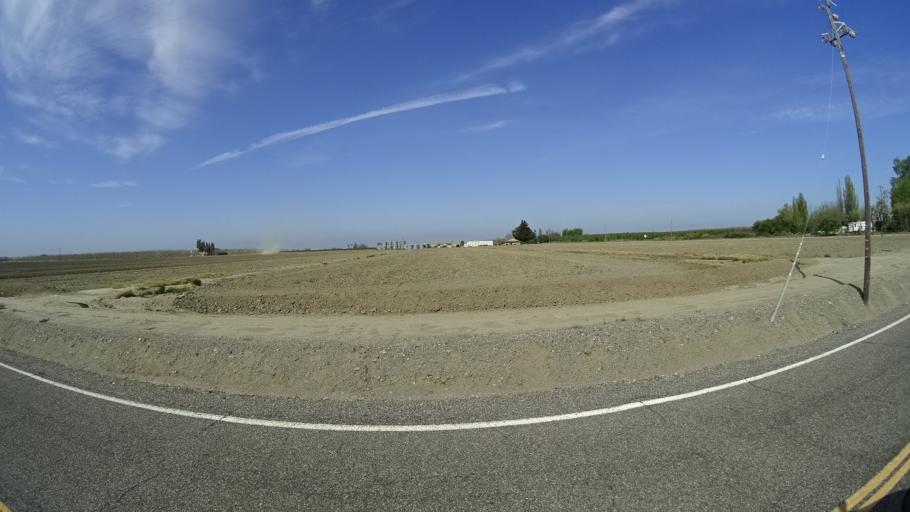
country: US
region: California
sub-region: Glenn County
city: Hamilton City
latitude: 39.6263
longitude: -122.0369
